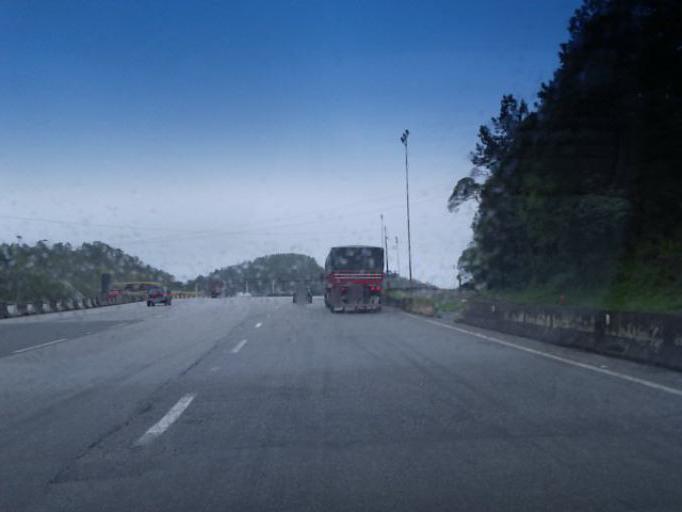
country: BR
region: Parana
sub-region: Campina Grande Do Sul
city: Campina Grande do Sul
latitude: -25.2913
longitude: -48.9341
